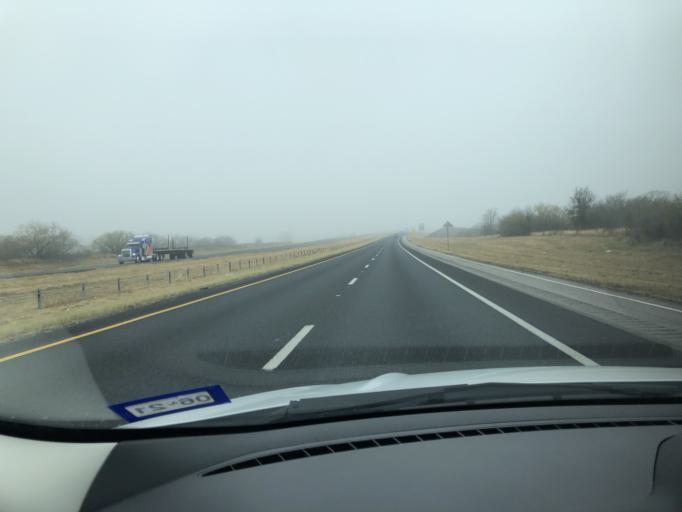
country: US
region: Texas
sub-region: Gonzales County
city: Waelder
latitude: 29.6596
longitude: -97.4058
